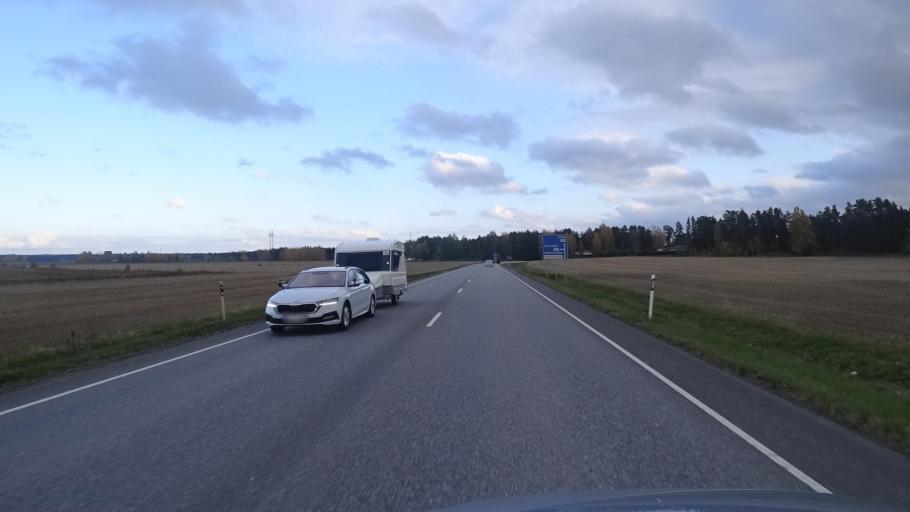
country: FI
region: Satakunta
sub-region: Rauma
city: Saekylae
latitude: 61.0408
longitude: 22.3796
